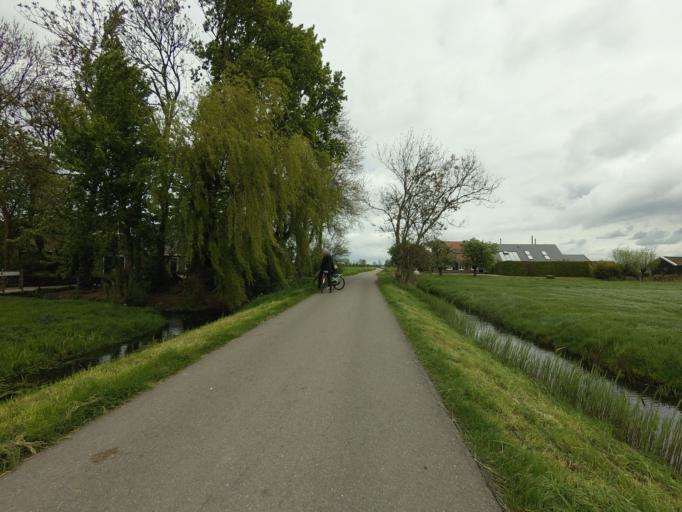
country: NL
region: North Holland
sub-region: Gemeente Weesp
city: Weesp
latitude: 52.3354
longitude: 5.0825
